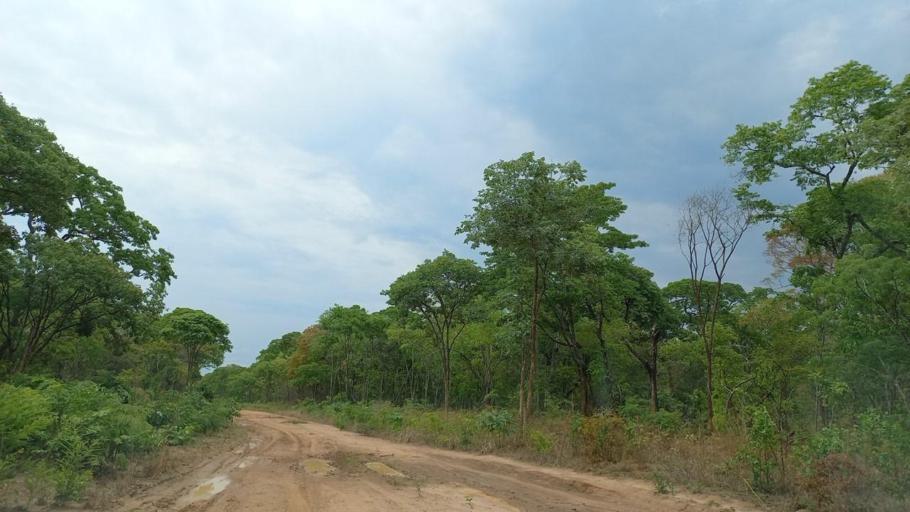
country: ZM
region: North-Western
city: Kalengwa
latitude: -13.5700
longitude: 24.9706
